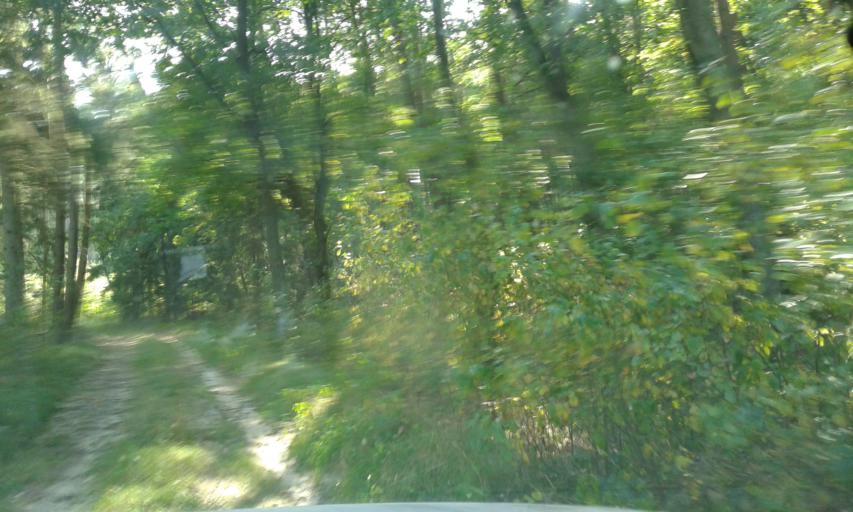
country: PL
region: West Pomeranian Voivodeship
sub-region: Powiat stargardzki
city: Suchan
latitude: 53.2481
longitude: 15.3460
